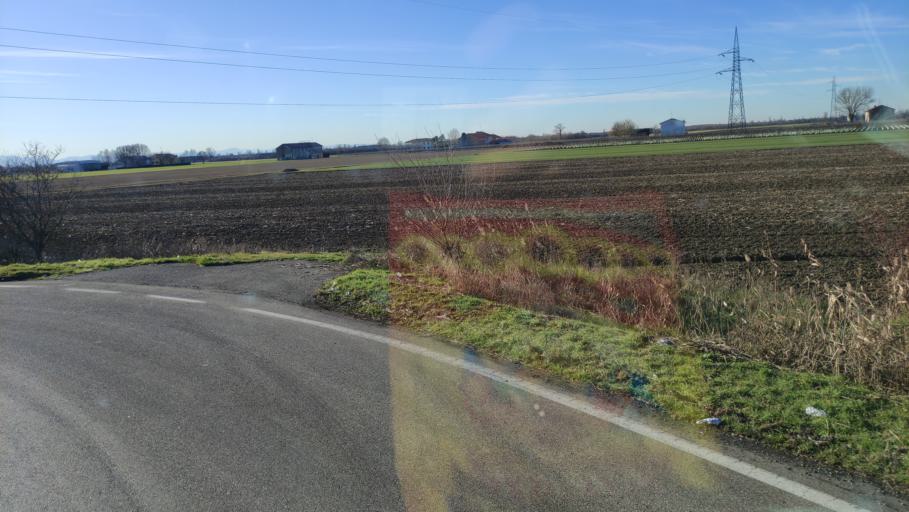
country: IT
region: Emilia-Romagna
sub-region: Provincia di Reggio Emilia
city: Novellara
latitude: 44.8294
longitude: 10.6982
